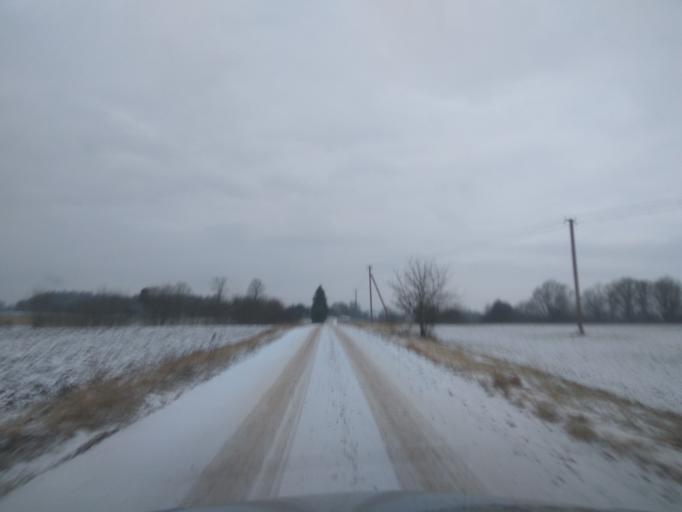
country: LV
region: Aizpute
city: Aizpute
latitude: 56.7180
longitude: 21.6426
